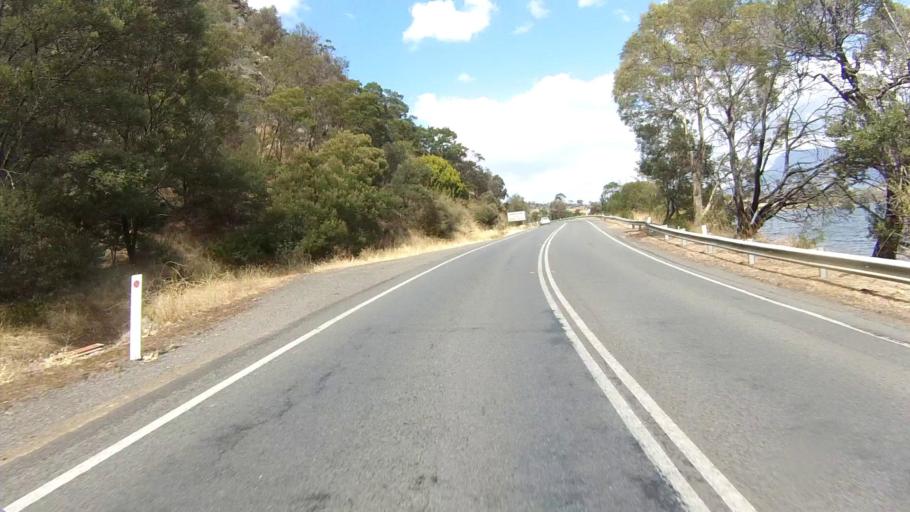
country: AU
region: Tasmania
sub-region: Brighton
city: Old Beach
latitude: -42.7862
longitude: 147.2911
